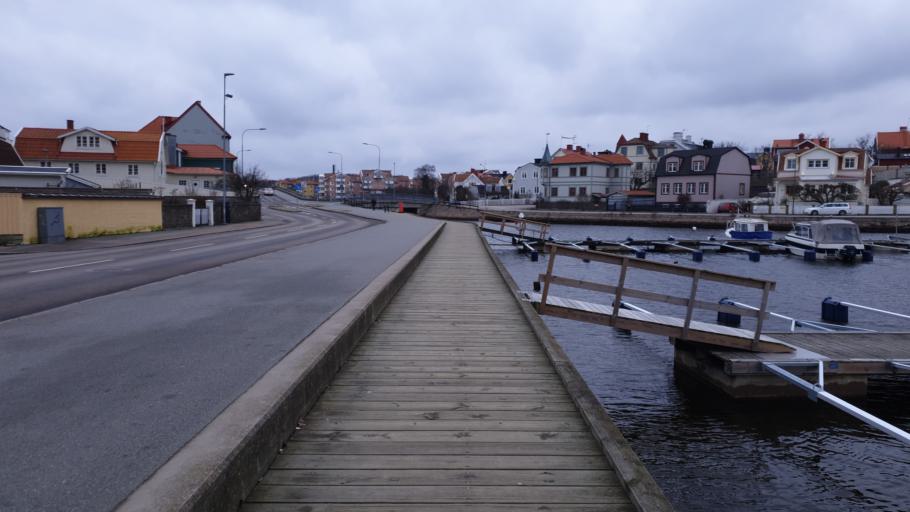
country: SE
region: Blekinge
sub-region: Karlskrona Kommun
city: Karlskrona
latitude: 56.1635
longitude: 15.5742
